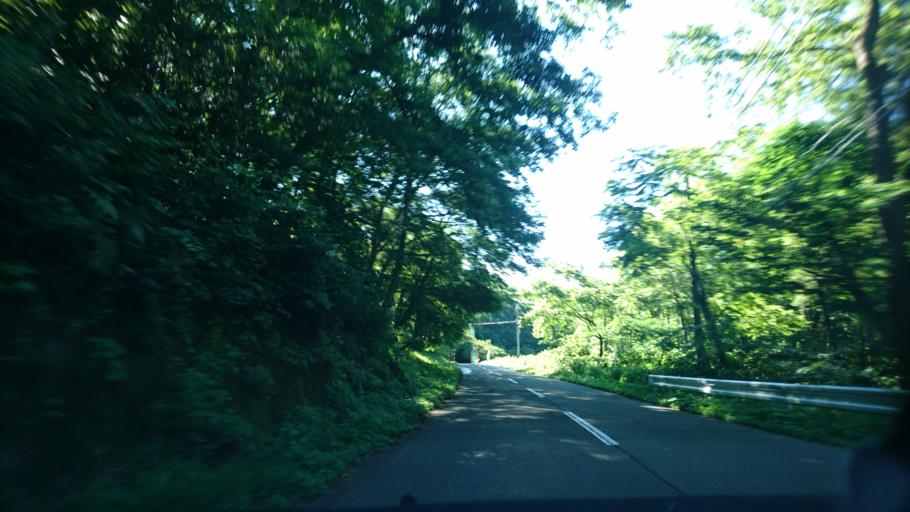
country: JP
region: Akita
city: Kakunodatemachi
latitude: 39.7158
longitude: 140.6245
